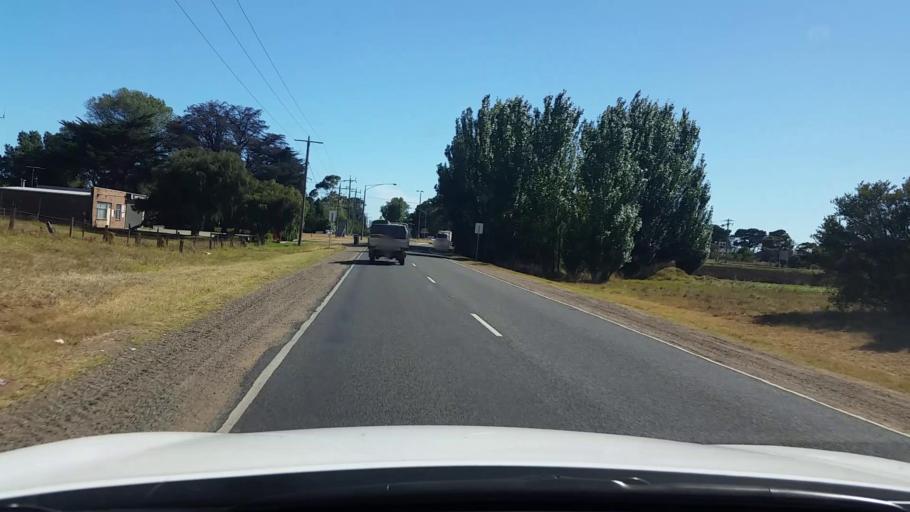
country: AU
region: Victoria
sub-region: Mornington Peninsula
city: Rosebud West
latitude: -38.3996
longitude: 144.8880
